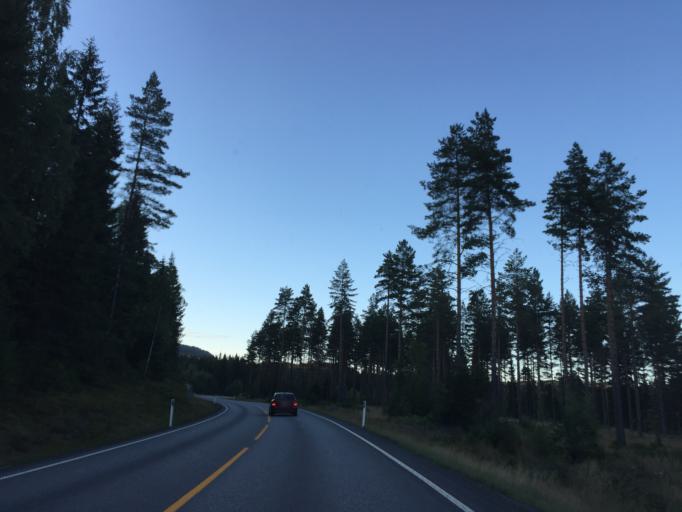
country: NO
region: Hedmark
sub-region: Nord-Odal
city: Sand
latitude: 60.4943
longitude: 11.5019
